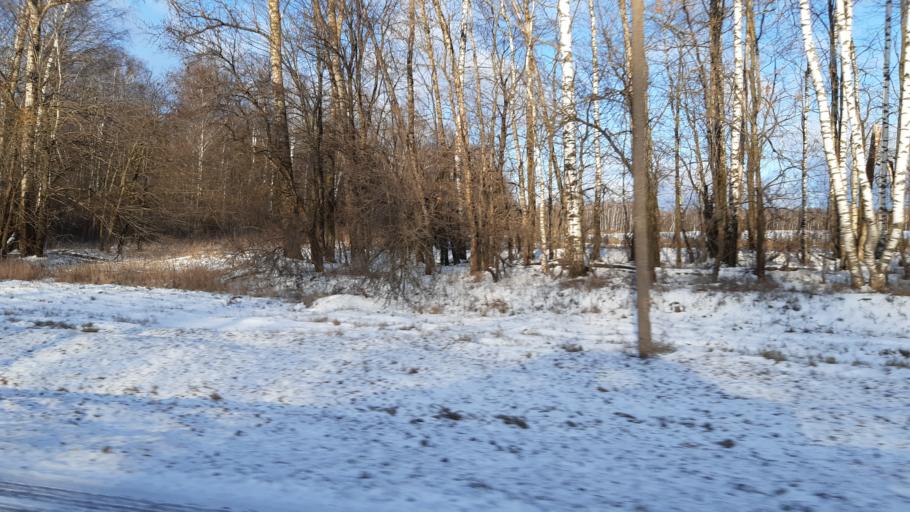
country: RU
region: Vladimir
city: Arsaki
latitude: 56.2909
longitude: 38.3822
